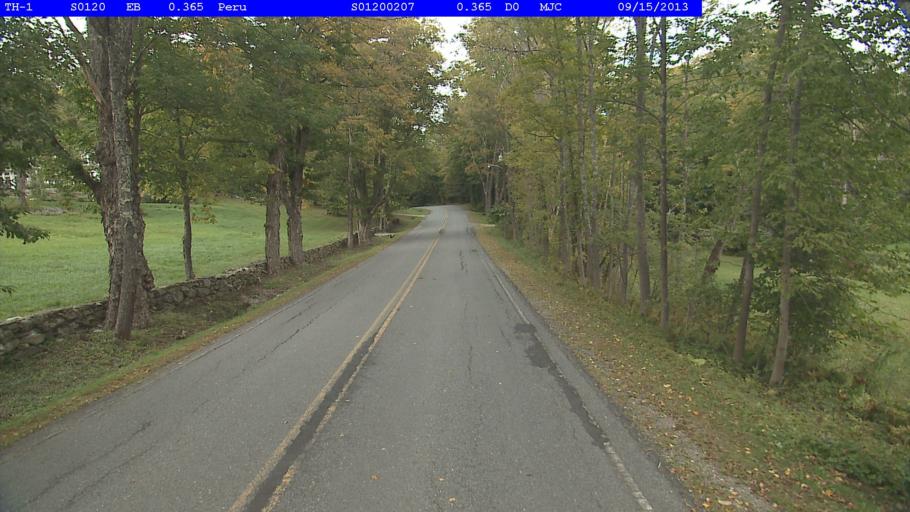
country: US
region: Vermont
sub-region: Bennington County
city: Manchester Center
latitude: 43.2312
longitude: -72.8989
